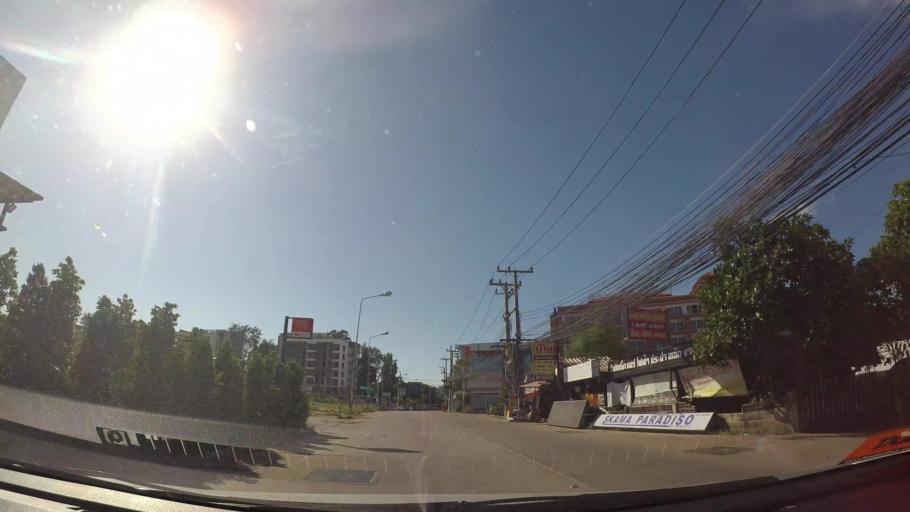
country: TH
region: Chon Buri
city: Phatthaya
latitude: 12.9093
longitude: 100.8811
